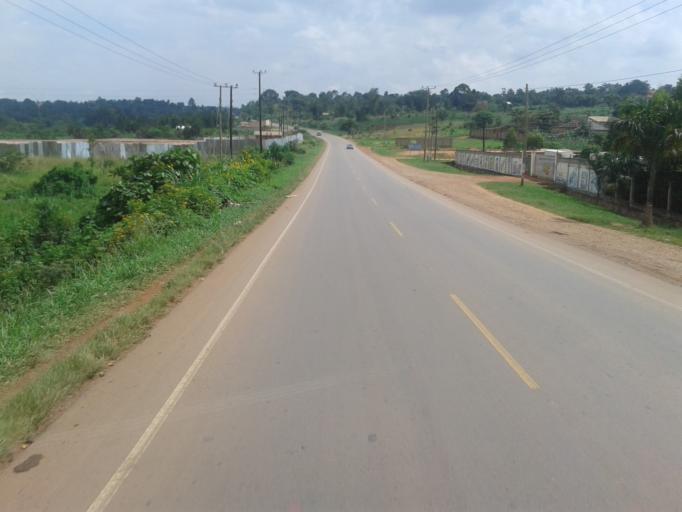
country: UG
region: Central Region
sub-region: Wakiso District
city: Wakiso
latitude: 0.4683
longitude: 32.5189
